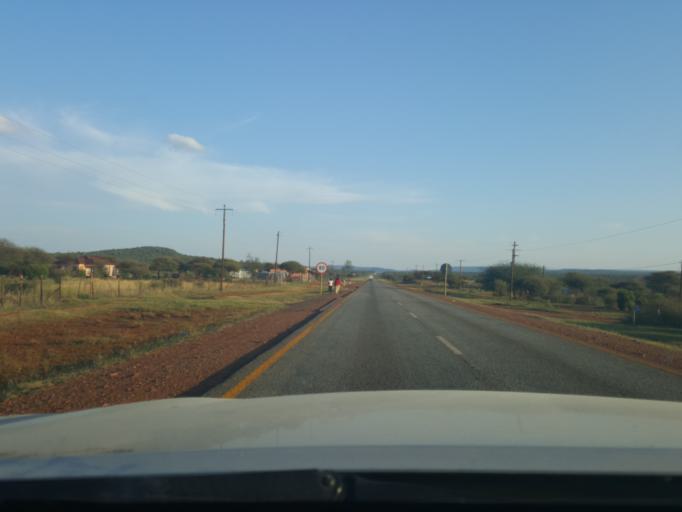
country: ZA
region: North-West
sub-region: Ngaka Modiri Molema District Municipality
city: Zeerust
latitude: -25.3925
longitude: 26.0844
